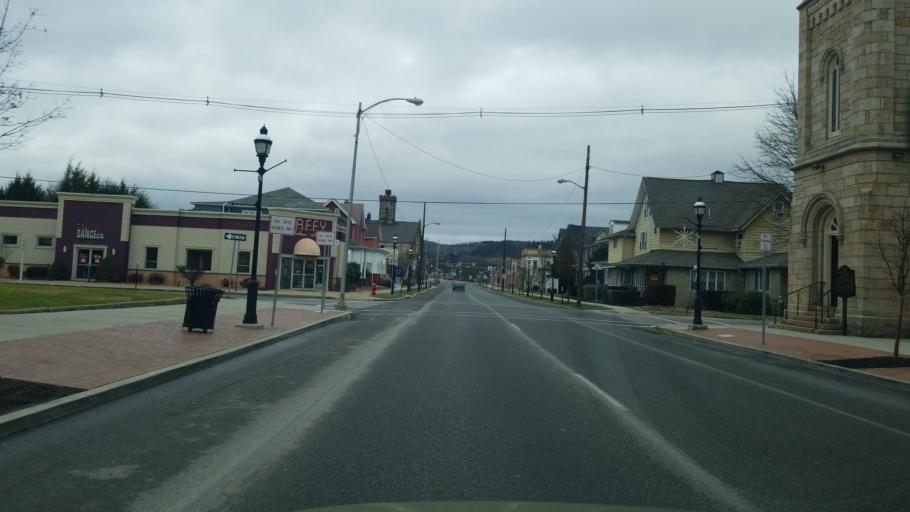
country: US
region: Pennsylvania
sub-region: Clearfield County
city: Clearfield
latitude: 41.0240
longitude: -78.4381
